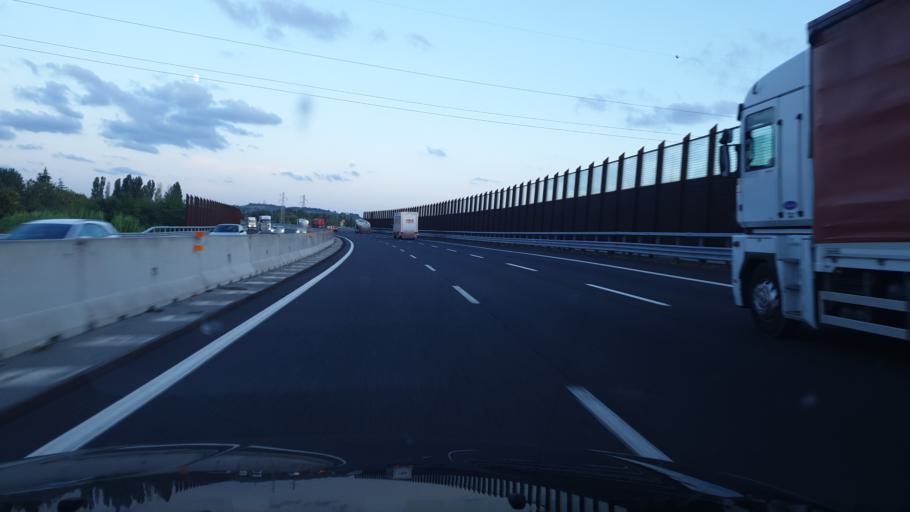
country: IT
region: Emilia-Romagna
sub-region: Provincia di Rimini
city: Santa Giustina
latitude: 44.0656
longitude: 12.4952
